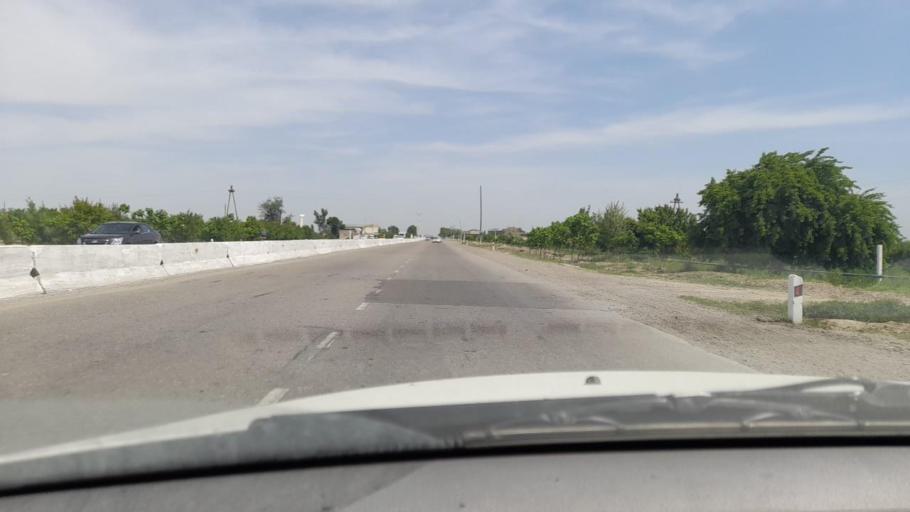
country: UZ
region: Bukhara
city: Galaosiyo
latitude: 39.8795
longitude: 64.4599
